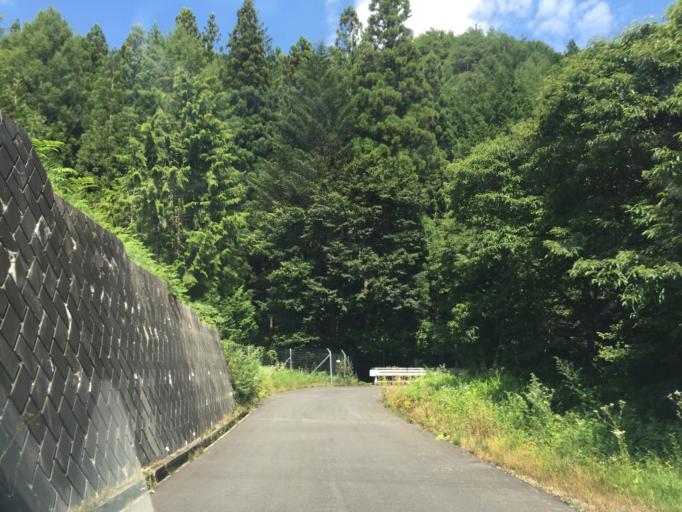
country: JP
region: Nagano
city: Iida
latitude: 35.3779
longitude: 137.6931
